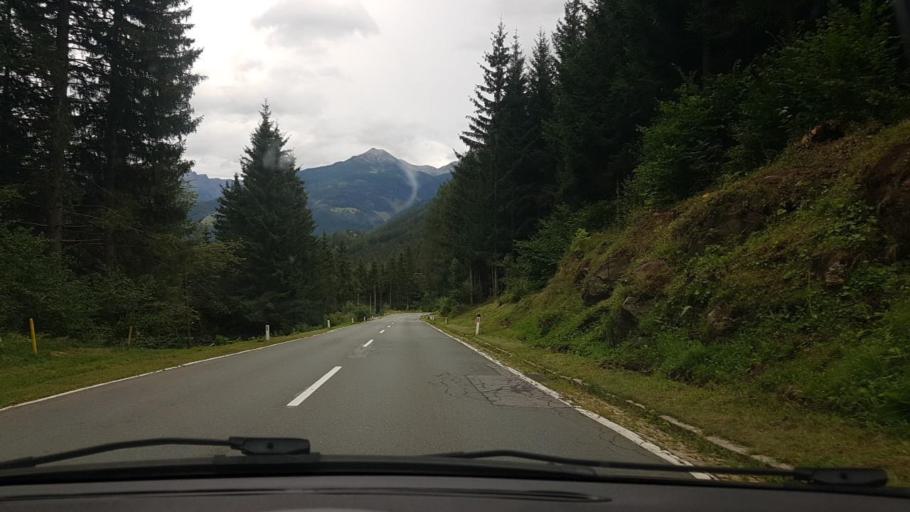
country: AT
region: Carinthia
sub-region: Politischer Bezirk Spittal an der Drau
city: Winklern
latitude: 46.8638
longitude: 12.8725
